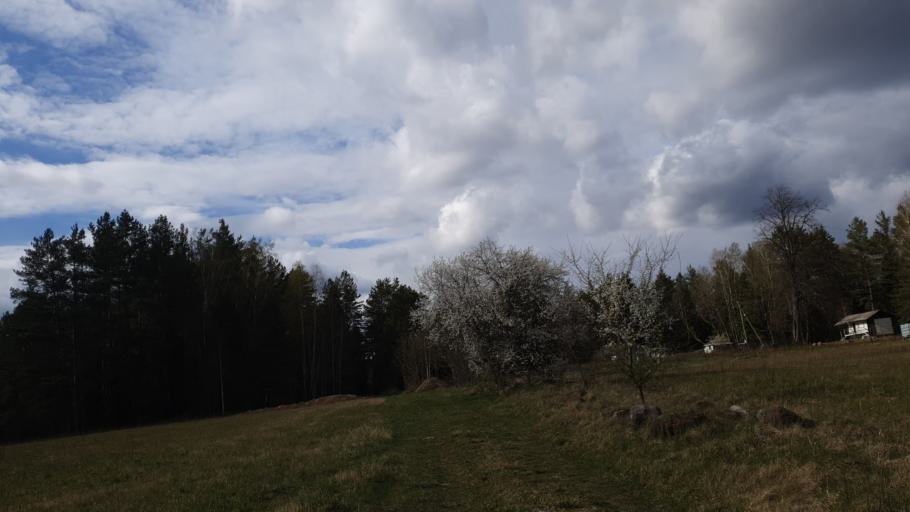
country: LT
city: Aukstadvaris
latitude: 54.5161
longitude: 24.6451
